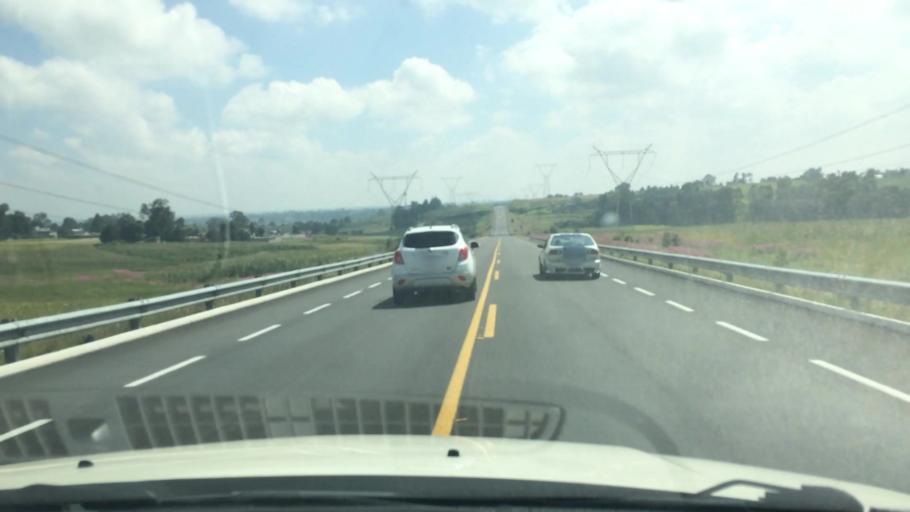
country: MX
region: Mexico
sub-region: Almoloya de Juarez
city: San Pedro de la Hortaliza (Ejido Almoloyan)
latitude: 19.3780
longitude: -99.8422
